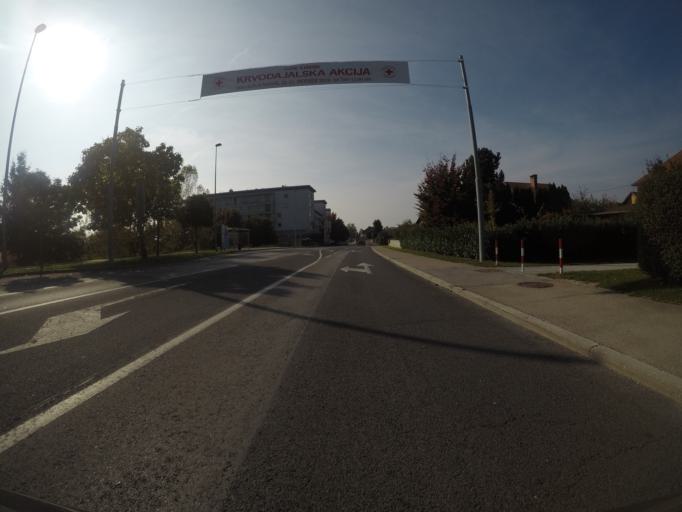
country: SI
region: Kamnik
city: Kamnik
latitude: 46.2152
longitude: 14.6022
